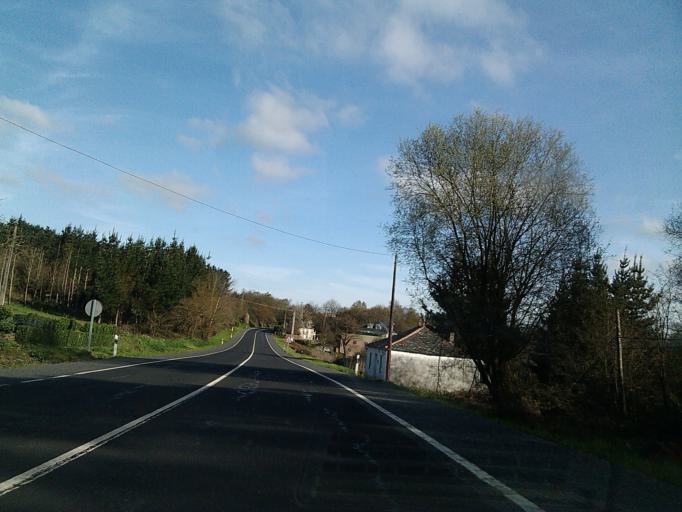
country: ES
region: Galicia
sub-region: Provincia de Lugo
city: Outeiro de Rei
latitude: 43.0721
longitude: -7.6031
